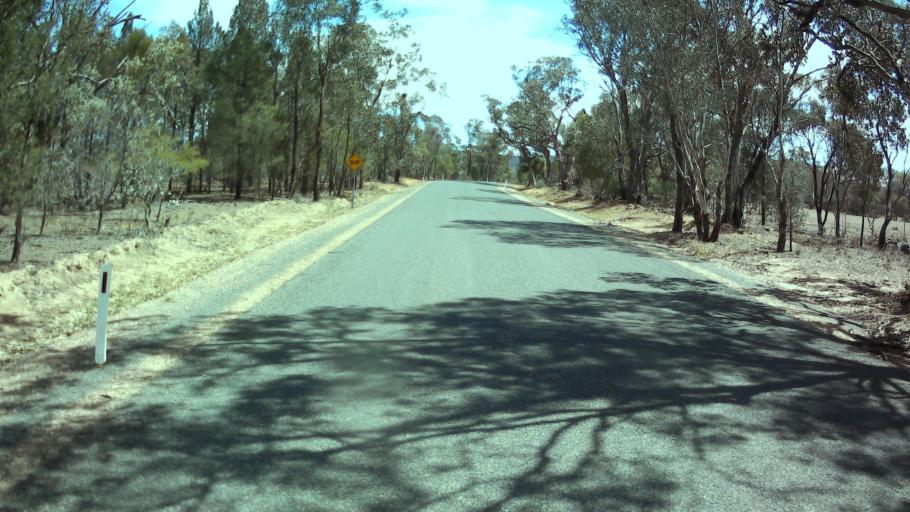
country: AU
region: New South Wales
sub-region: Weddin
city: Grenfell
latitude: -33.7691
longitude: 148.2048
